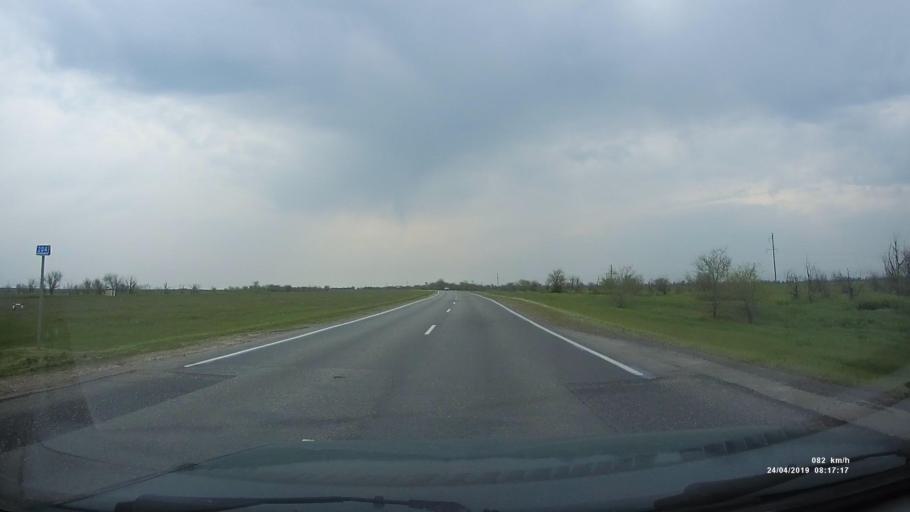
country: RU
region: Kalmykiya
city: Priyutnoye
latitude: 46.0980
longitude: 43.6272
